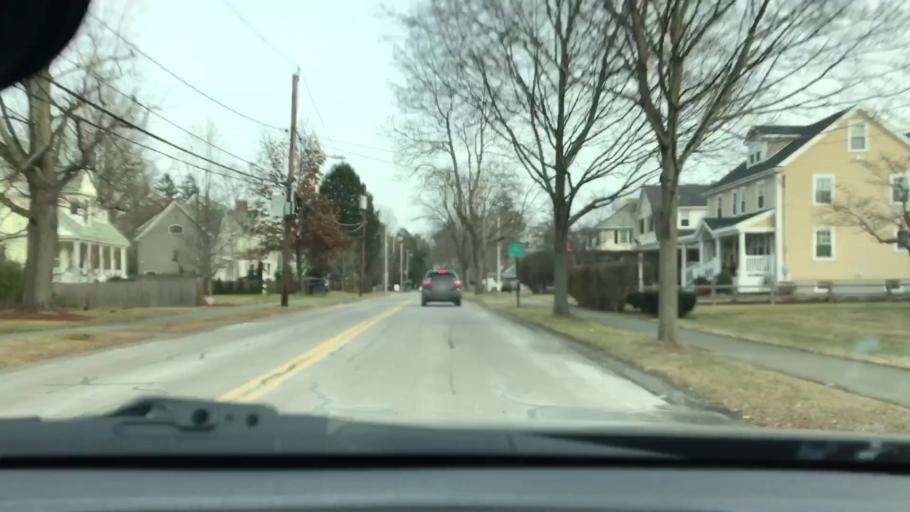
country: US
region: Massachusetts
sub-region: Norfolk County
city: Needham
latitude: 42.2829
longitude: -71.2327
